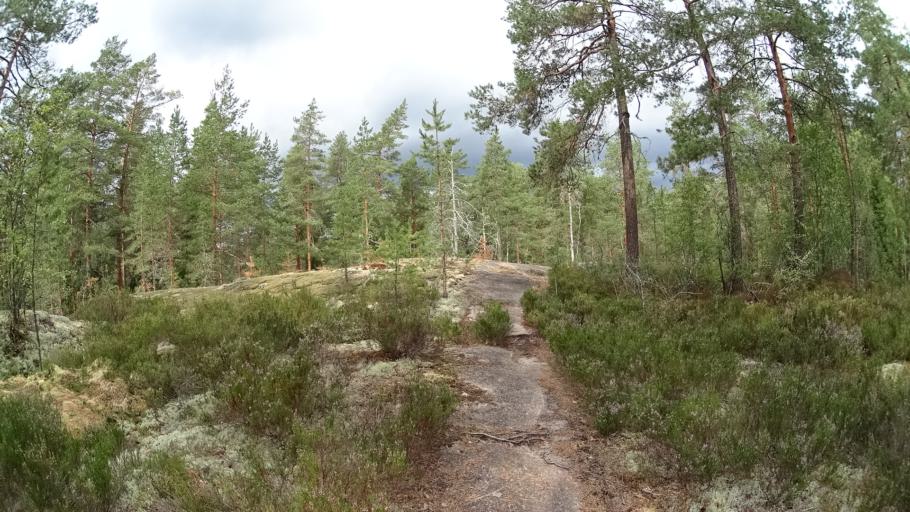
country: FI
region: Uusimaa
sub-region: Helsinki
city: Espoo
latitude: 60.3059
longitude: 24.5791
